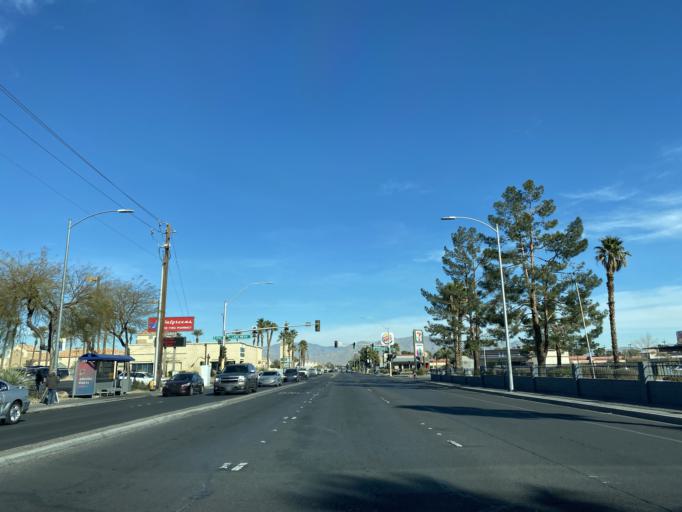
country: US
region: Nevada
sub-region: Clark County
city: Las Vegas
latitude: 36.1951
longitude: -115.2239
